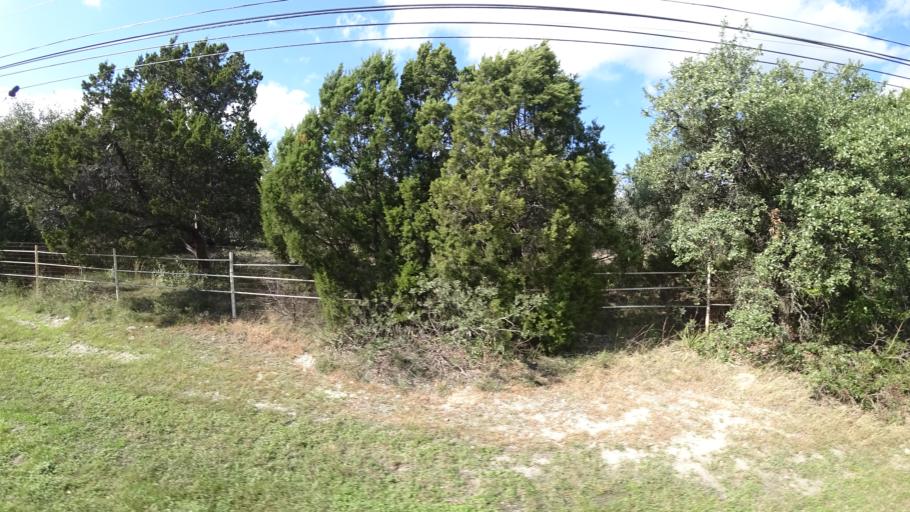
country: US
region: Texas
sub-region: Travis County
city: Barton Creek
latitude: 30.2580
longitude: -97.8888
